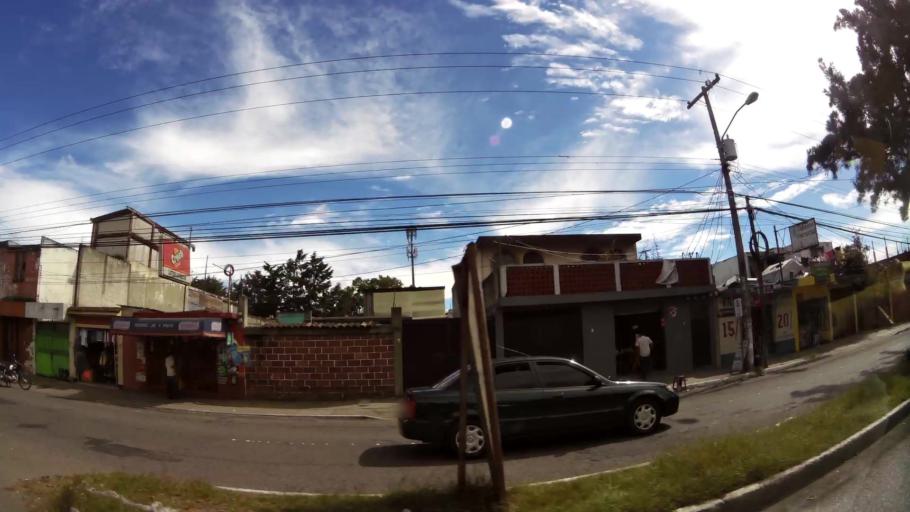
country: GT
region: Guatemala
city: Mixco
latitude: 14.6452
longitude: -90.5805
